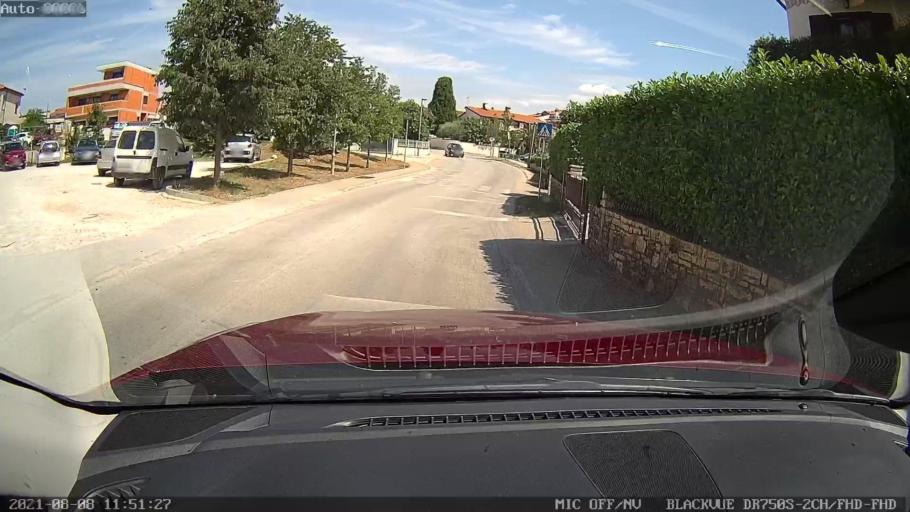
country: HR
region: Istarska
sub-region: Grad Rovinj
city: Rovinj
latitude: 45.0826
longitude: 13.6470
